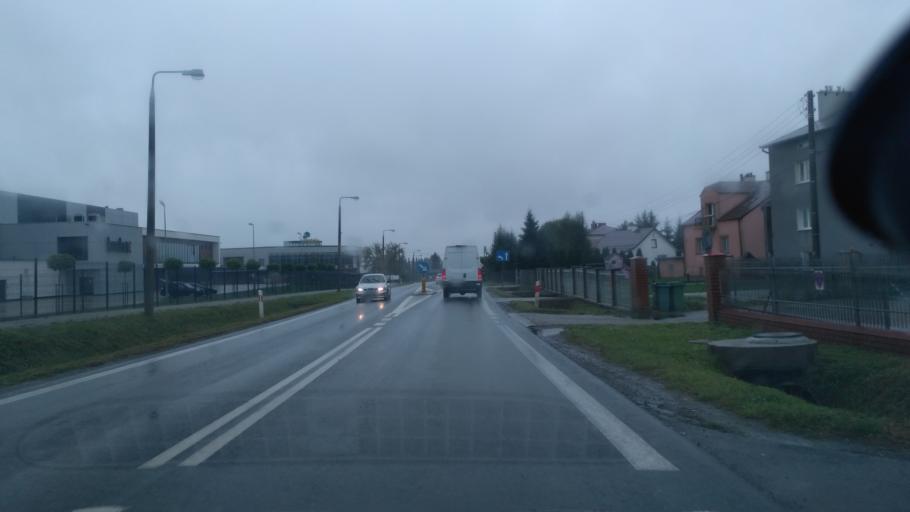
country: PL
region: Subcarpathian Voivodeship
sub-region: Powiat debicki
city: Debica
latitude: 50.0597
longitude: 21.4459
